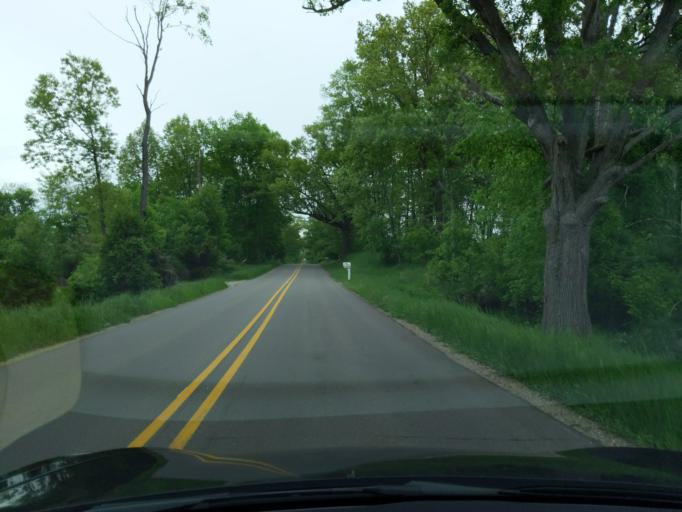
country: US
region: Michigan
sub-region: Jackson County
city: Jackson
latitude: 42.3430
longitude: -84.3486
